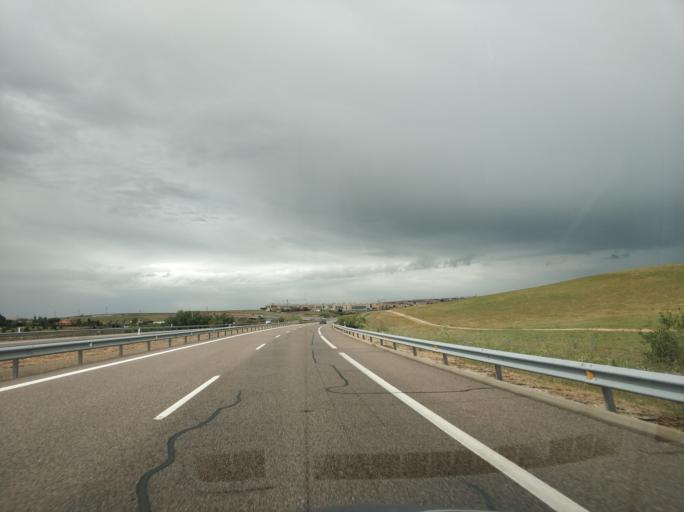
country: ES
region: Castille and Leon
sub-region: Provincia de Salamanca
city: Aldeatejada
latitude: 40.9324
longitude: -5.6794
